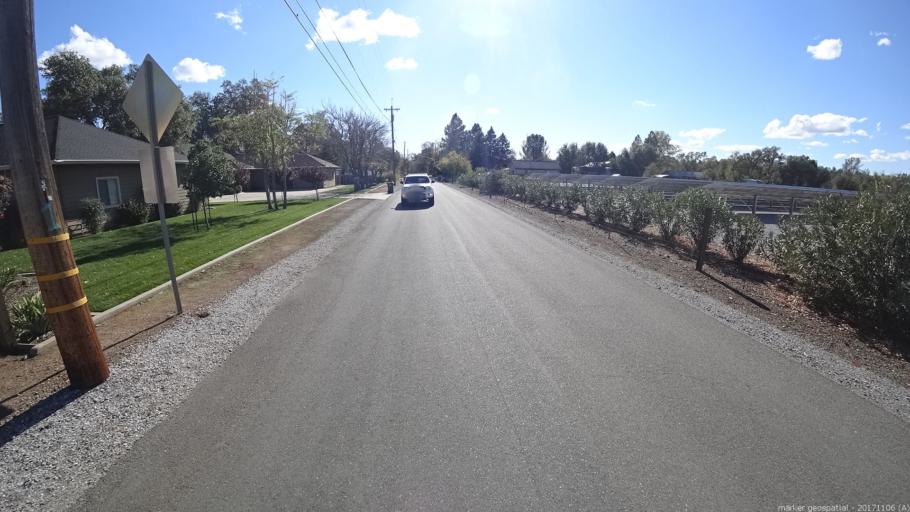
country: US
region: California
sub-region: Shasta County
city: Palo Cedro
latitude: 40.5873
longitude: -122.2969
